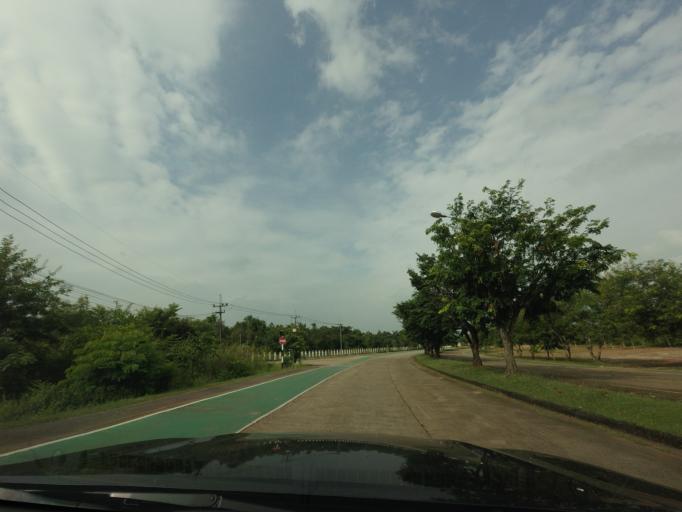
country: TH
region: Nong Khai
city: Nong Khai
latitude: 17.8119
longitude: 102.7462
